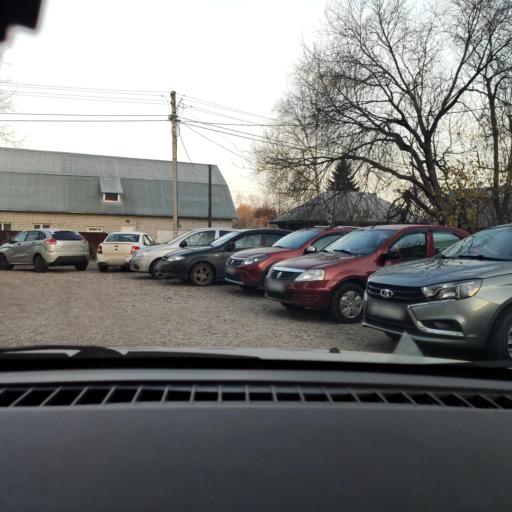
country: RU
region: Perm
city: Perm
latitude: 58.0674
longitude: 56.3400
